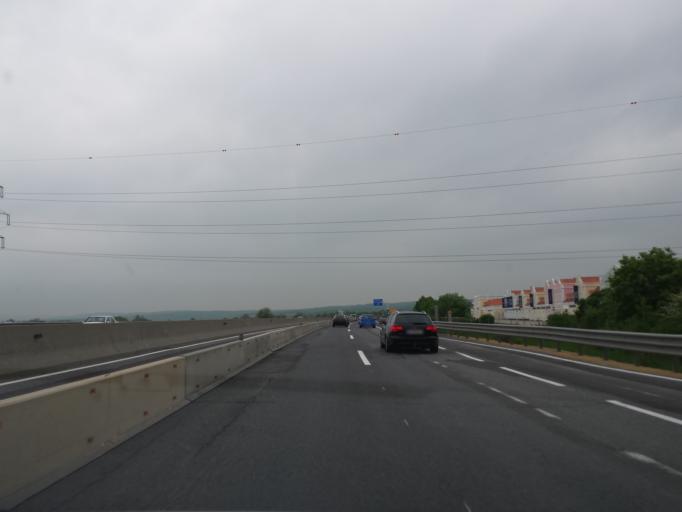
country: AT
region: Burgenland
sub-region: Politischer Bezirk Neusiedl am See
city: Parndorf
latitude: 47.9757
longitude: 16.8533
